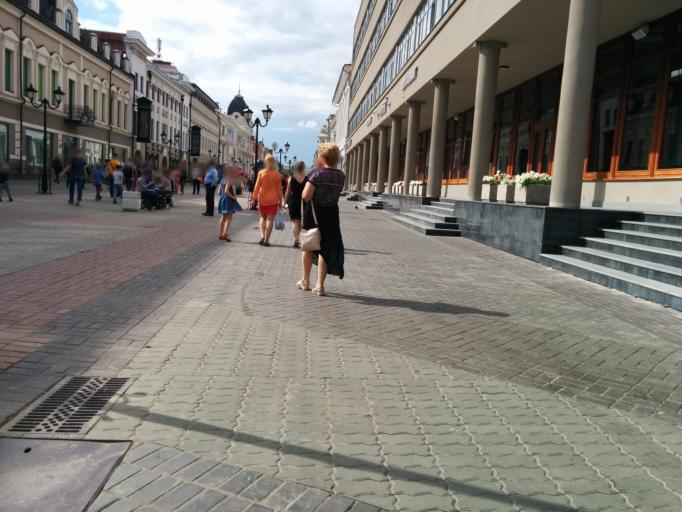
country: RU
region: Tatarstan
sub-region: Gorod Kazan'
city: Kazan
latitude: 55.7910
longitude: 49.1145
